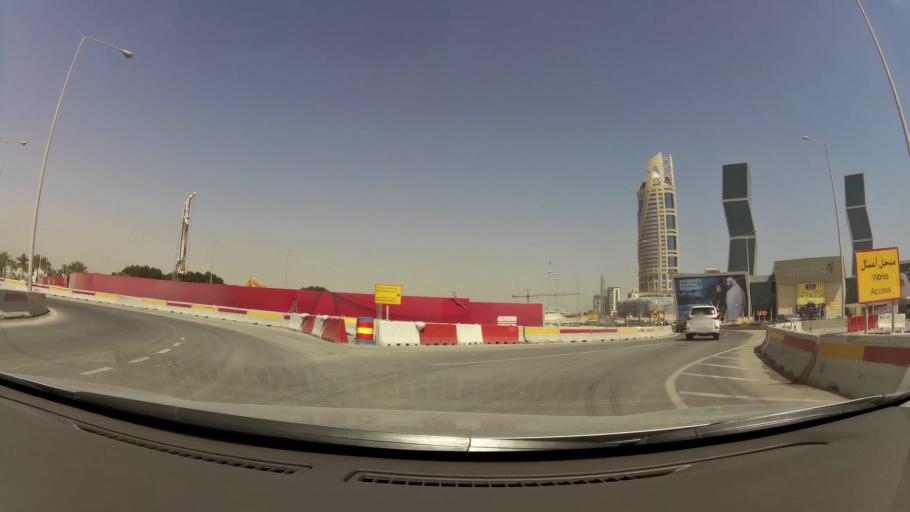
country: QA
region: Baladiyat ad Dawhah
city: Doha
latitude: 25.3735
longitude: 51.5239
